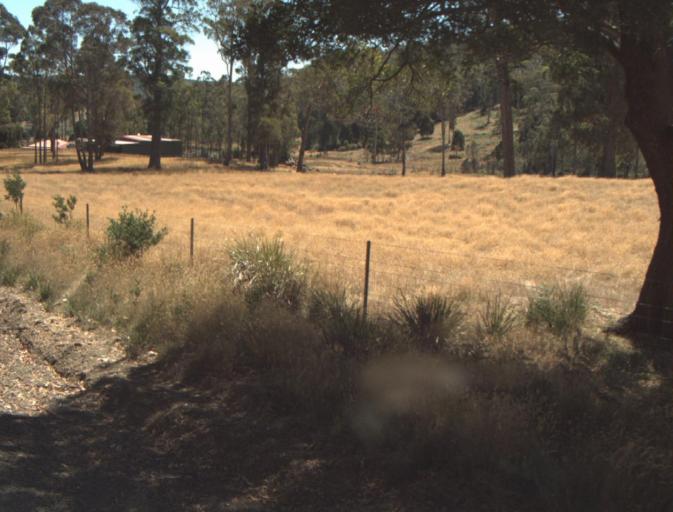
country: AU
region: Tasmania
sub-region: Launceston
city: Newstead
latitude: -41.3454
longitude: 147.3714
